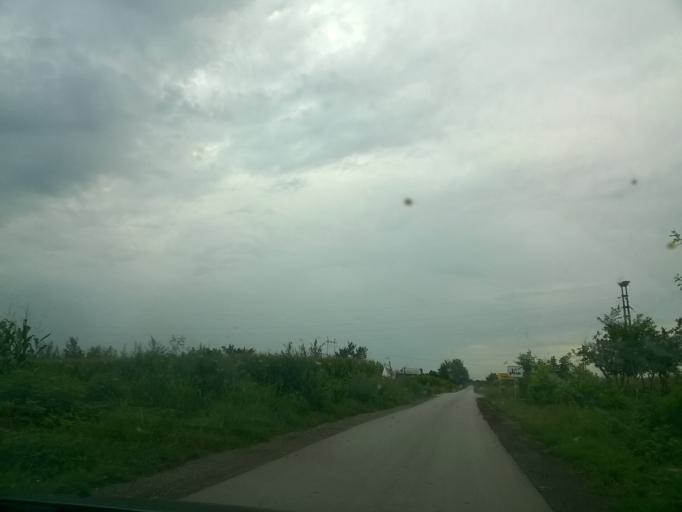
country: RS
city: Tomasevac
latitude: 45.2791
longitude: 20.6320
